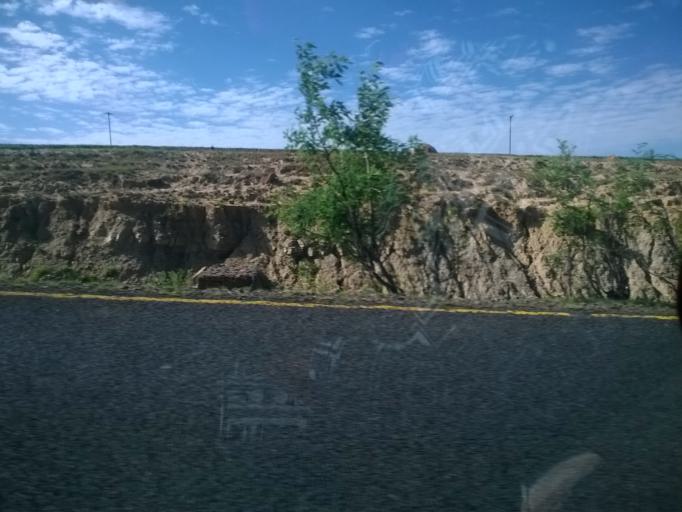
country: LS
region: Berea
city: Teyateyaneng
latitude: -29.0854
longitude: 27.9179
